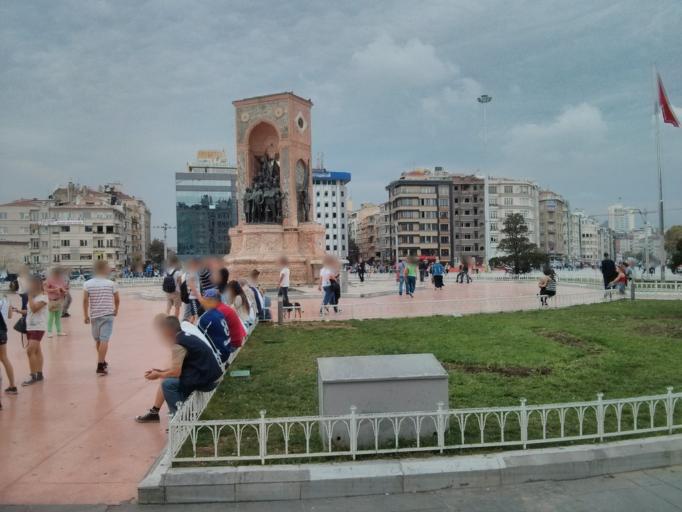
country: TR
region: Istanbul
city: Eminoenue
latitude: 41.0367
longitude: 28.9853
